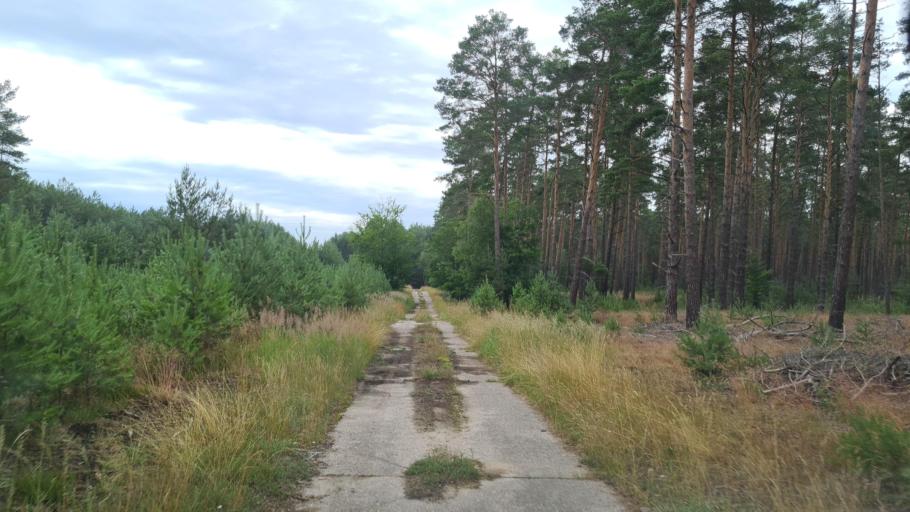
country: DE
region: Brandenburg
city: Crinitz
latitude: 51.7216
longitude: 13.7274
